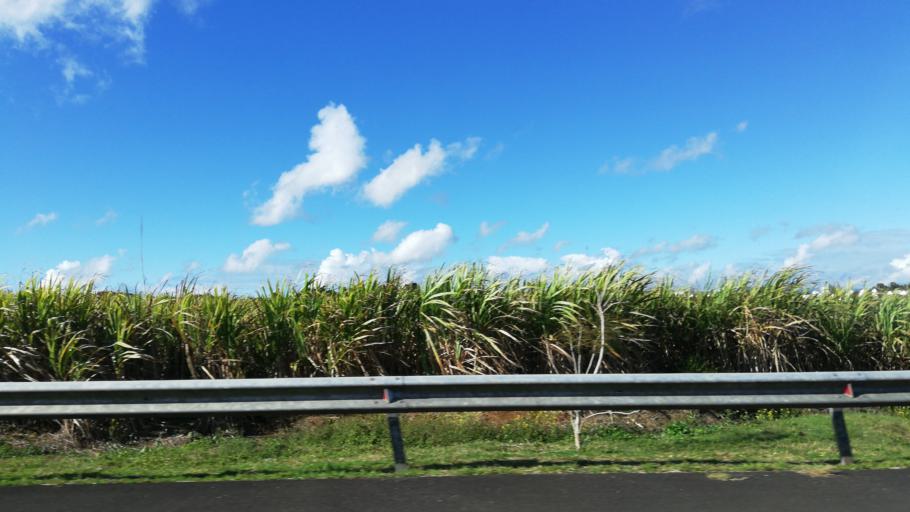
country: MU
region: Moka
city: Saint Pierre
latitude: -20.2324
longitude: 57.5196
